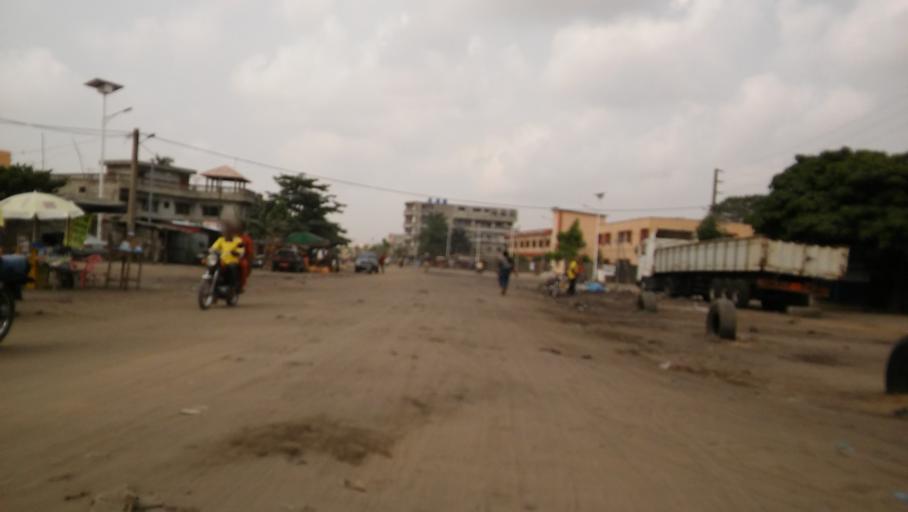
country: BJ
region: Littoral
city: Cotonou
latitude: 6.3909
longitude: 2.3799
